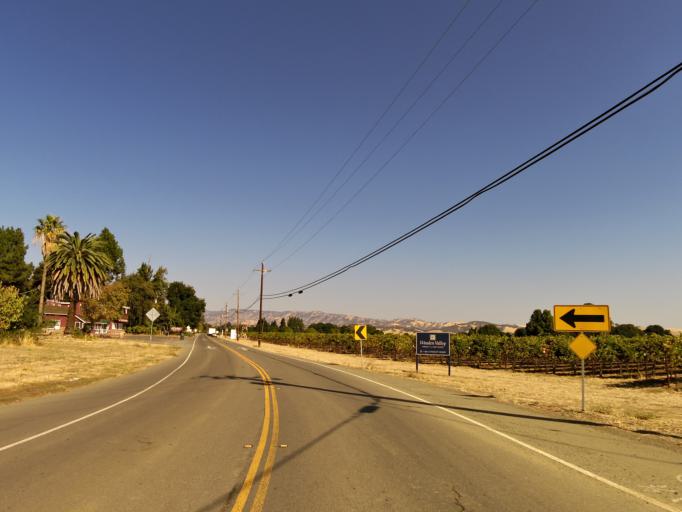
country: US
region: California
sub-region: Solano County
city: Green Valley
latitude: 38.2628
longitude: -122.1138
